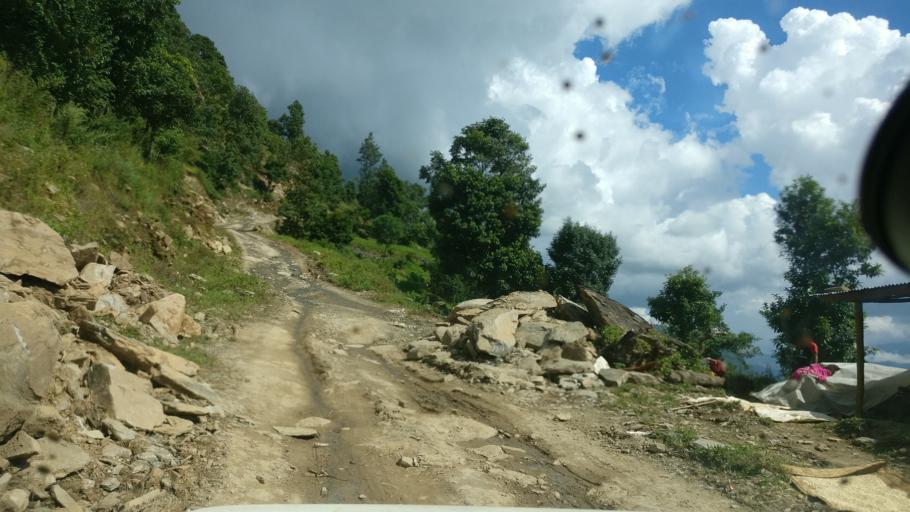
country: NP
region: Western Region
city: Baglung
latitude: 28.2643
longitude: 83.6409
